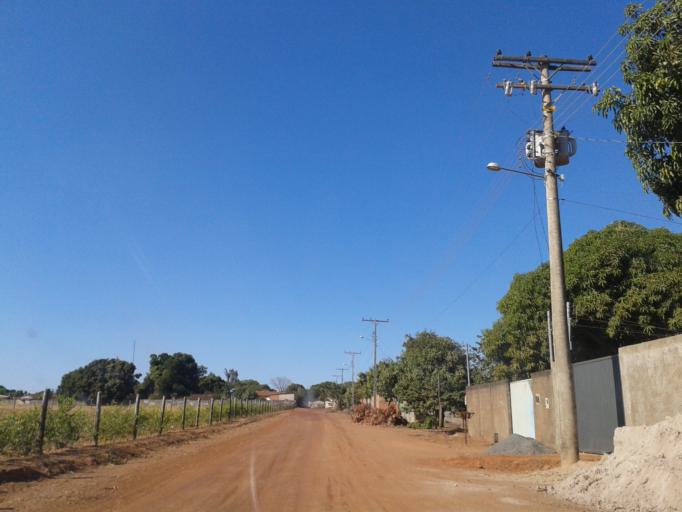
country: BR
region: Goias
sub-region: Sao Miguel Do Araguaia
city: Sao Miguel do Araguaia
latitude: -13.2855
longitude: -50.1787
